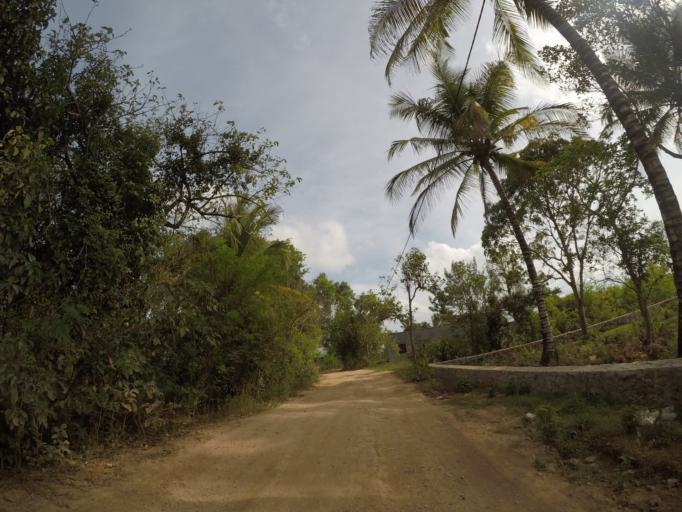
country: TZ
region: Zanzibar Central/South
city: Koani
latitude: -6.2278
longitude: 39.3190
